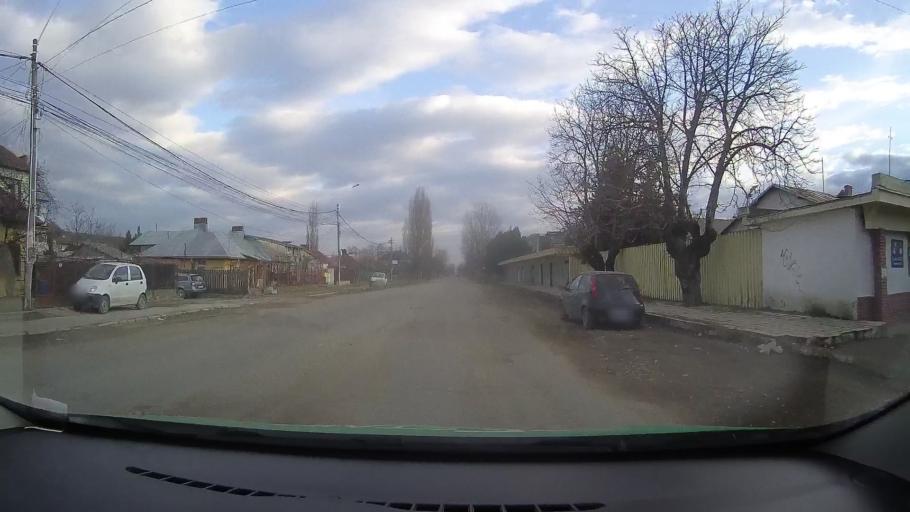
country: RO
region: Dambovita
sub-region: Municipiul Moreni
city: Moreni
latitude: 44.9714
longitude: 25.6507
